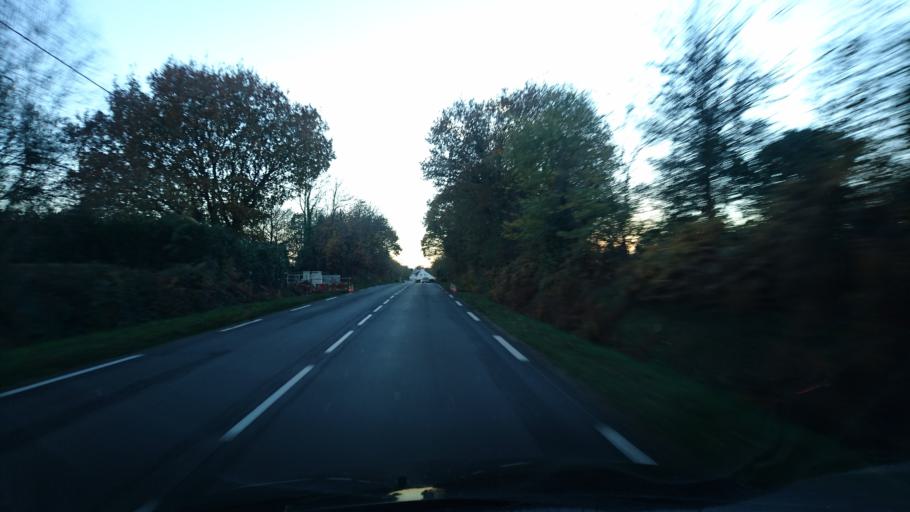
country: FR
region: Brittany
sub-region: Departement du Finistere
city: Quimperle
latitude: 47.8567
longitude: -3.5665
